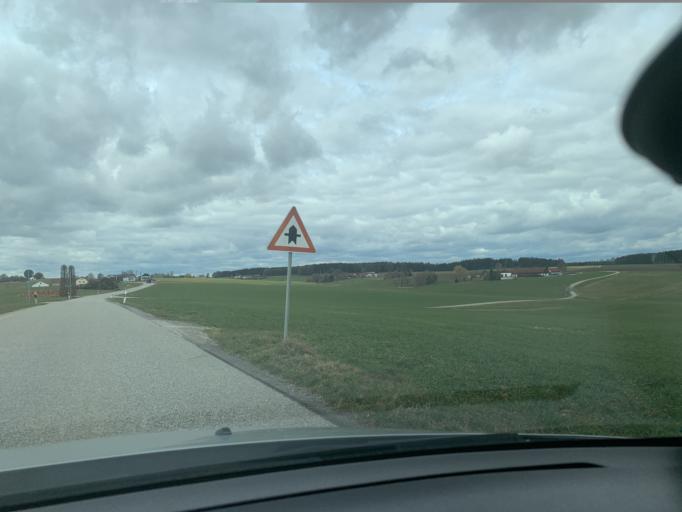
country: DE
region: Bavaria
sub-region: Lower Bavaria
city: Vilsbiburg
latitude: 48.4660
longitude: 12.3173
